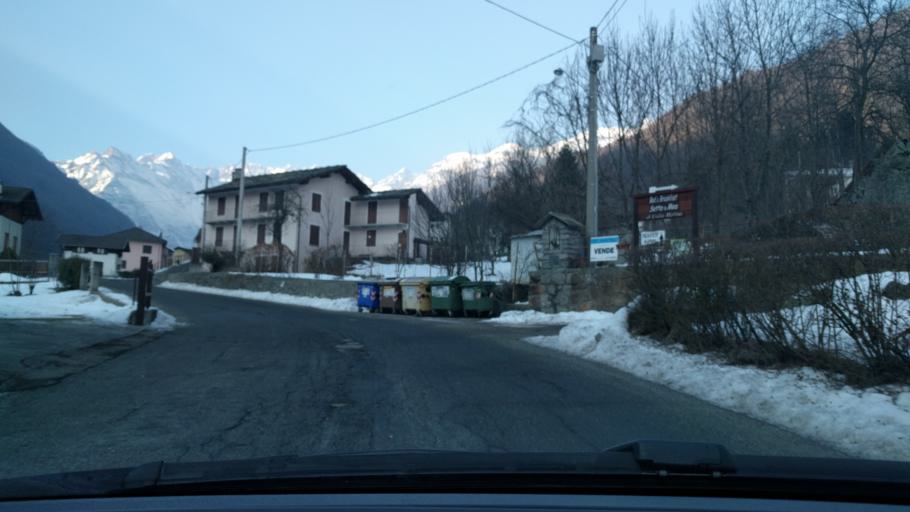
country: IT
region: Piedmont
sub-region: Provincia di Torino
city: Chialamberto
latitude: 45.3679
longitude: 7.3080
